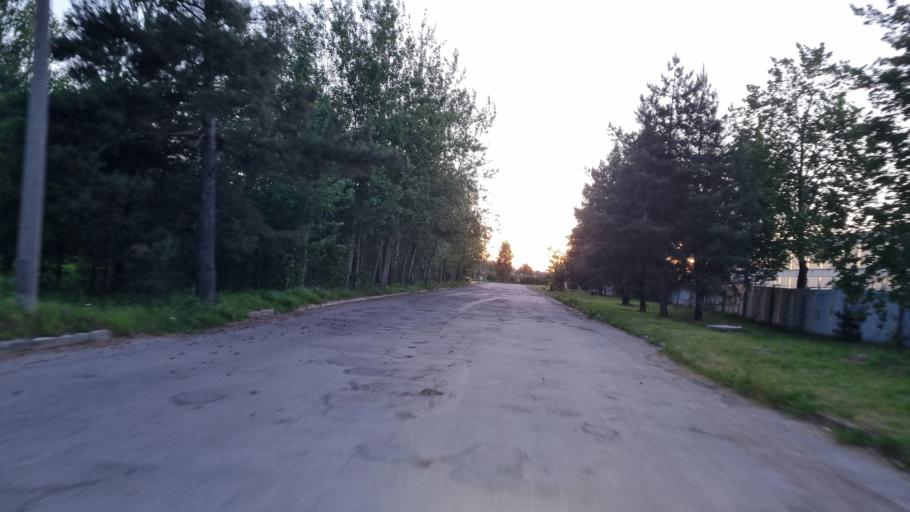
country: LV
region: Riga
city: Daugavgriva
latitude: 57.0238
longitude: 24.0277
